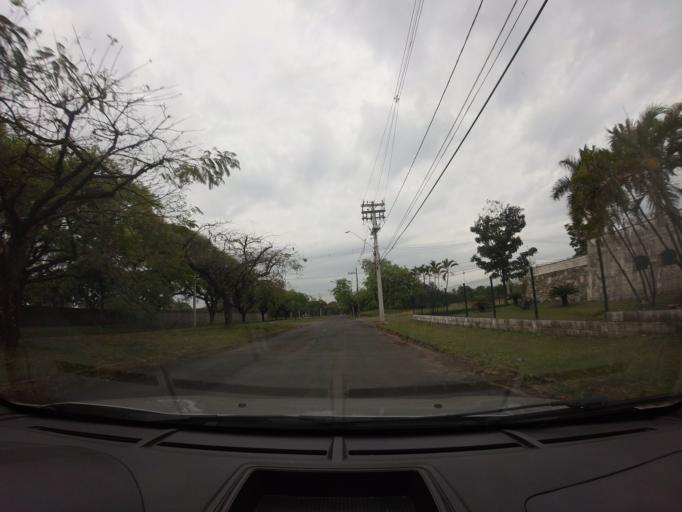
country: BR
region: Sao Paulo
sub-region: Piracicaba
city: Piracicaba
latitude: -22.7602
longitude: -47.5935
